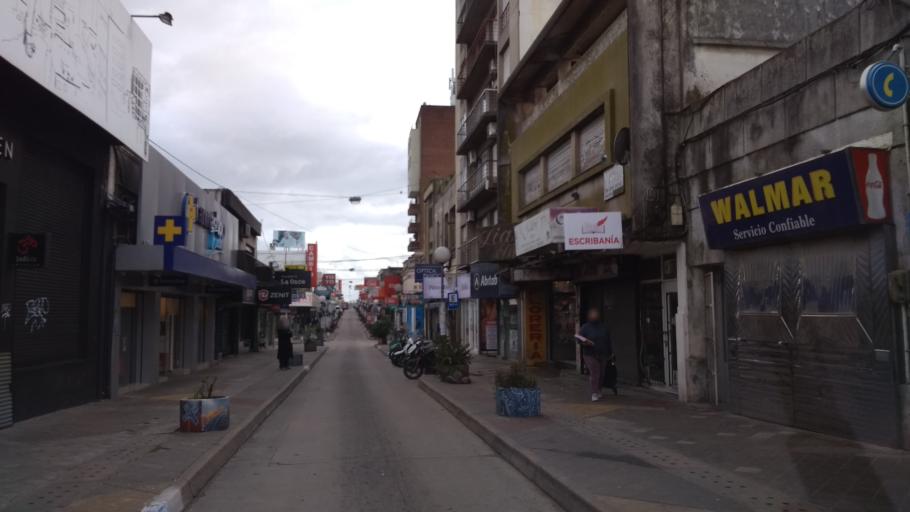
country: UY
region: Canelones
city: Pando
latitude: -34.7210
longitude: -55.9602
